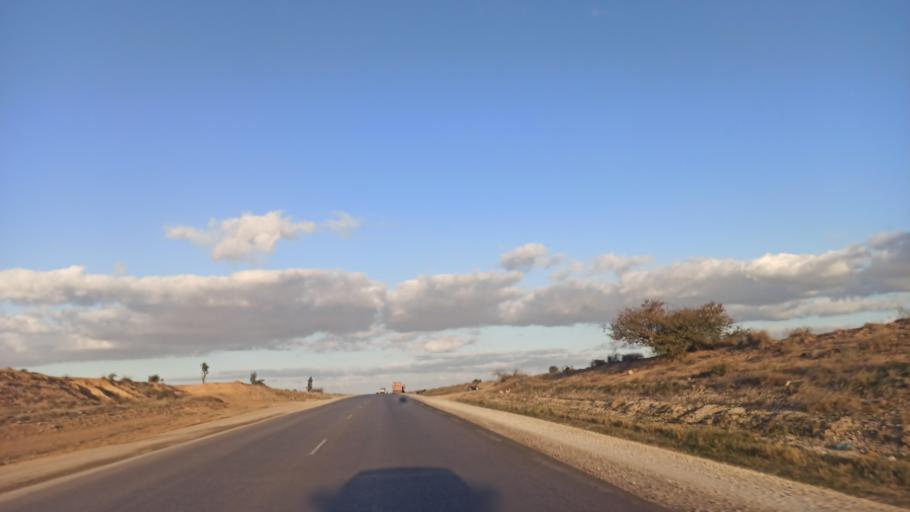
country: TN
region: Al Qayrawan
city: Sbikha
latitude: 35.8871
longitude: 10.2401
